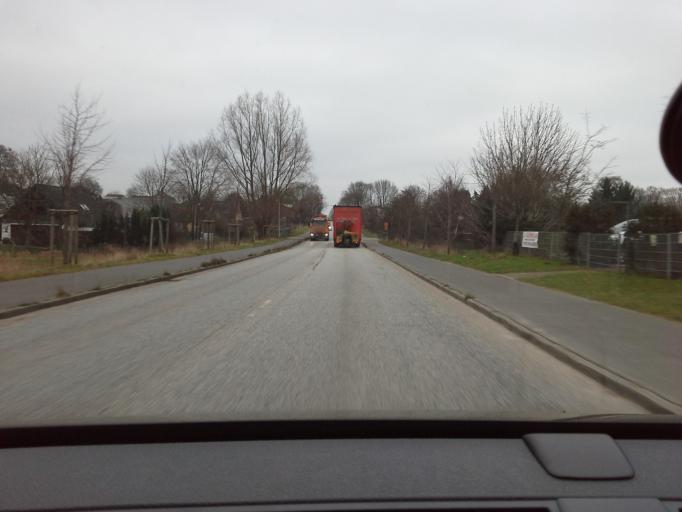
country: DE
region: Schleswig-Holstein
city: Lentfohrden
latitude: 53.8715
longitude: 9.8887
